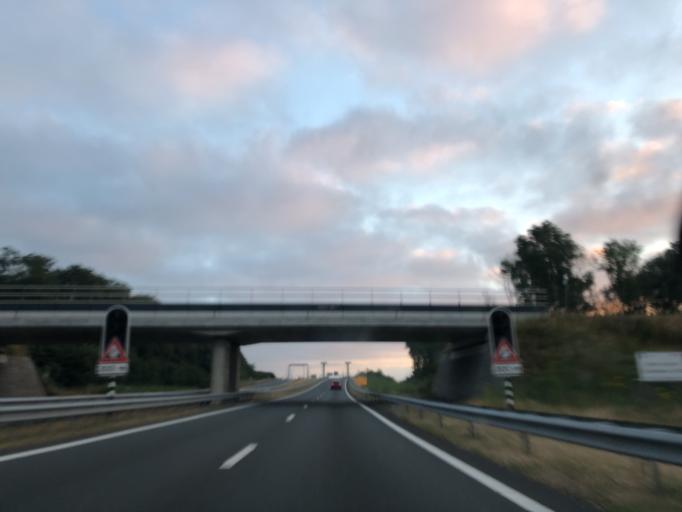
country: NL
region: Groningen
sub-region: Gemeente Veendam
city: Veendam
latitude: 53.1602
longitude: 6.8956
